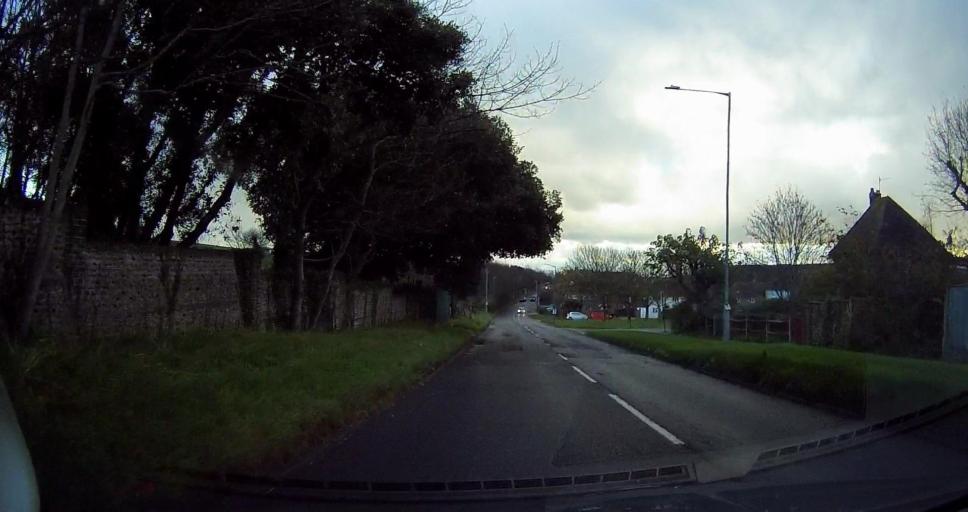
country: GB
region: England
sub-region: Brighton and Hove
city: Rottingdean
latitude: 50.8150
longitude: -0.0633
